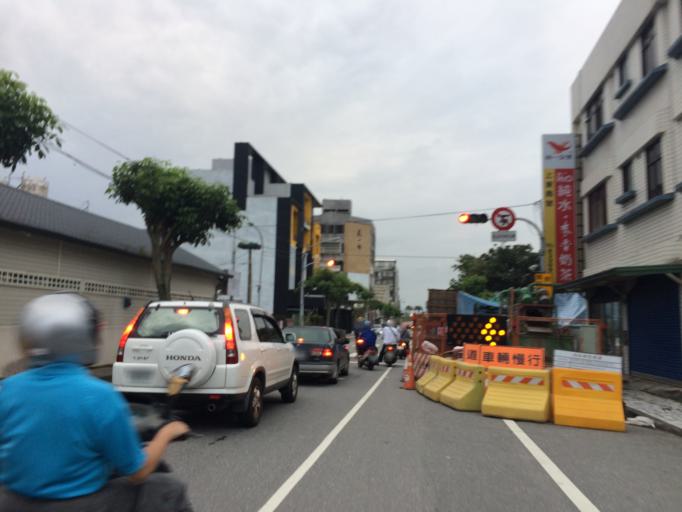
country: TW
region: Taiwan
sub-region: Hualien
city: Hualian
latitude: 23.9740
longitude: 121.6142
